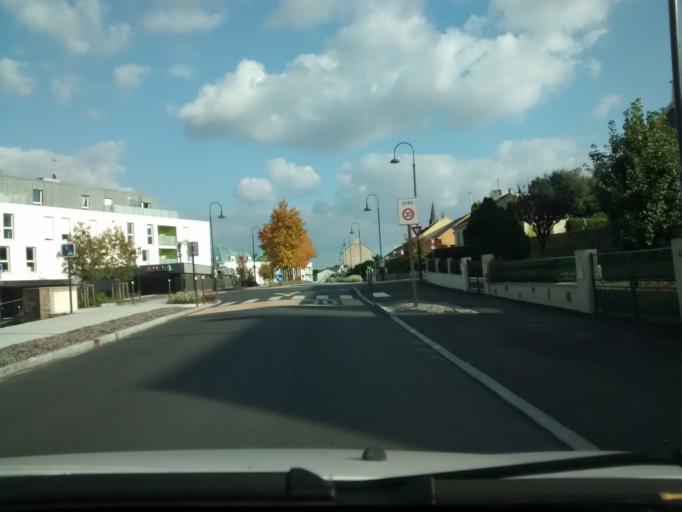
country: FR
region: Pays de la Loire
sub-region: Departement de la Loire-Atlantique
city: Orvault
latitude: 47.2724
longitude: -1.6274
